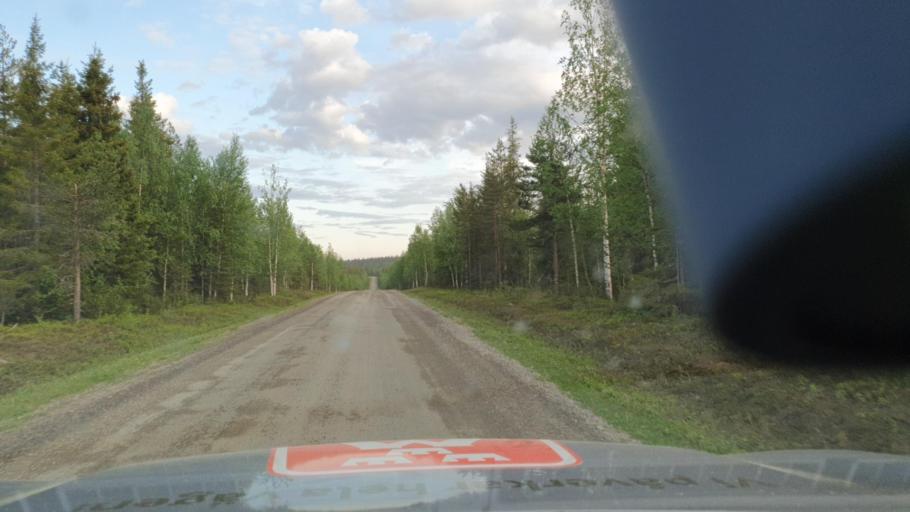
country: SE
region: Norrbotten
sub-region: Bodens Kommun
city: Boden
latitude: 66.5496
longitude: 21.4661
